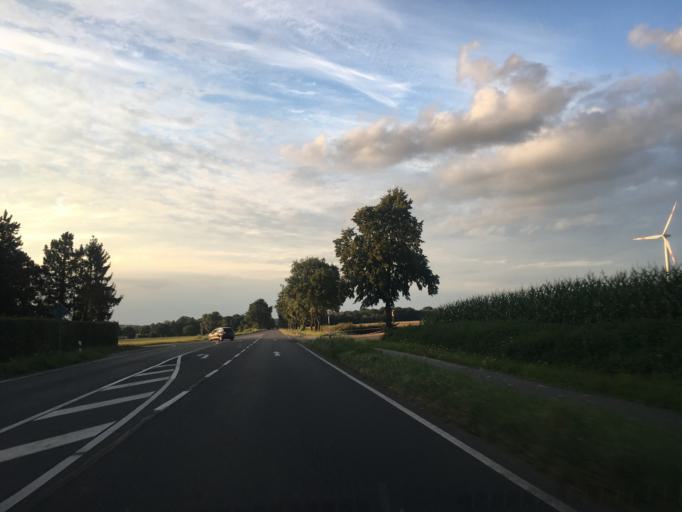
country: DE
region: North Rhine-Westphalia
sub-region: Regierungsbezirk Koln
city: Linnich
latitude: 51.0135
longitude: 6.2757
